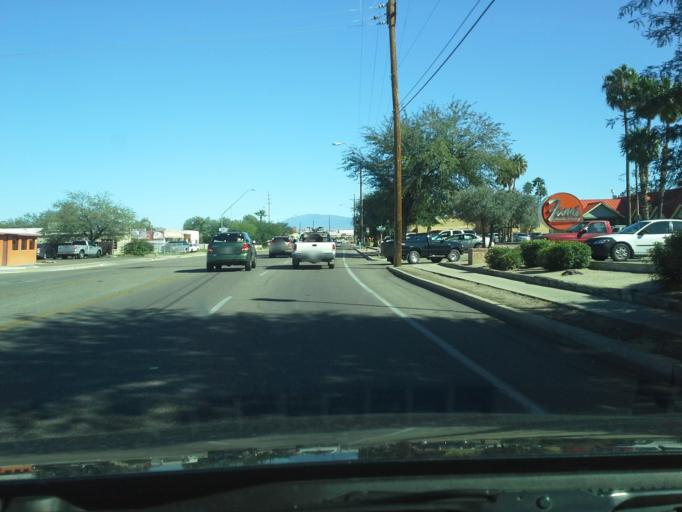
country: US
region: Arizona
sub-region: Pima County
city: South Tucson
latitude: 32.2297
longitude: -110.9882
